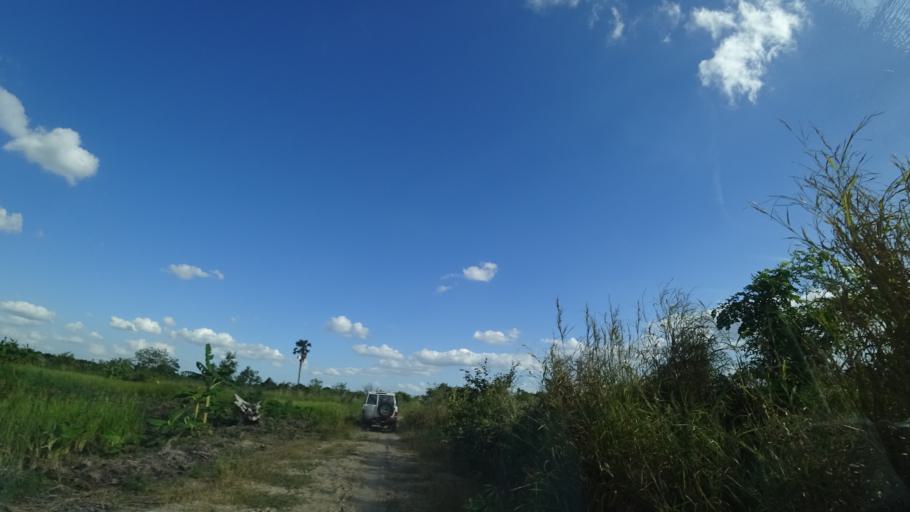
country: MZ
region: Sofala
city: Dondo
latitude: -19.3402
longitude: 34.5830
